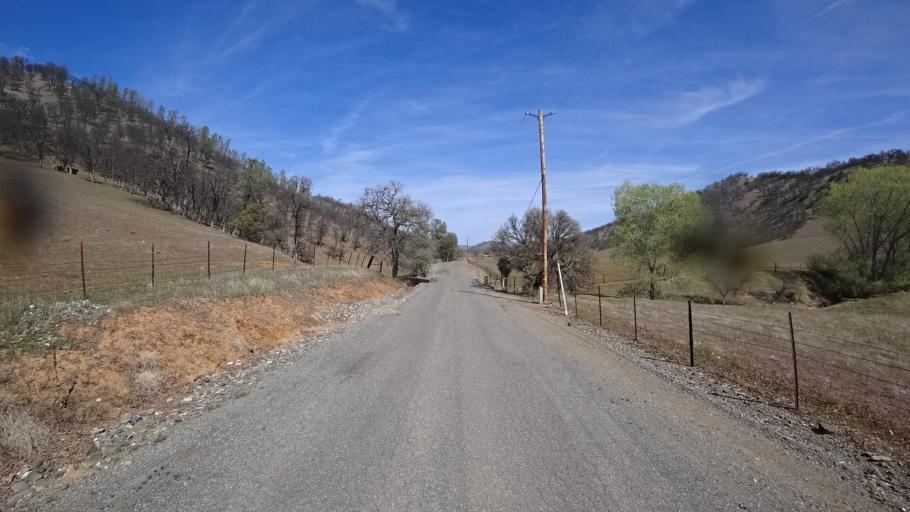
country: US
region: California
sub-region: Glenn County
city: Willows
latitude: 39.4946
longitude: -122.4541
